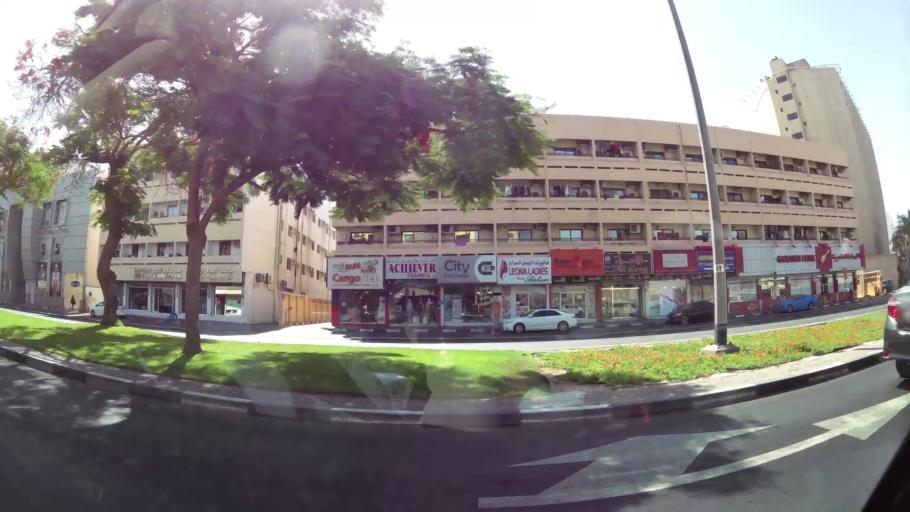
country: AE
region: Ash Shariqah
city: Sharjah
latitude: 25.2362
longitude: 55.2792
